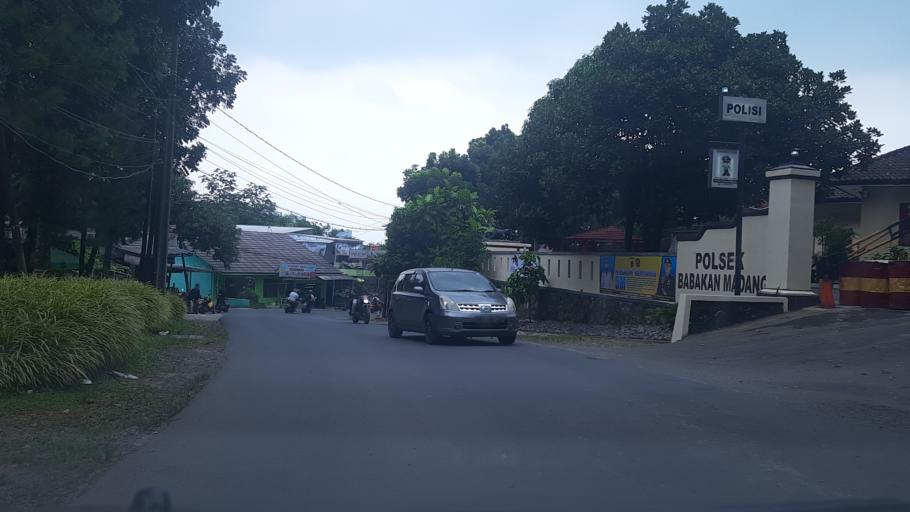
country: ID
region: West Java
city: Bogor
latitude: -6.5719
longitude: 106.8651
